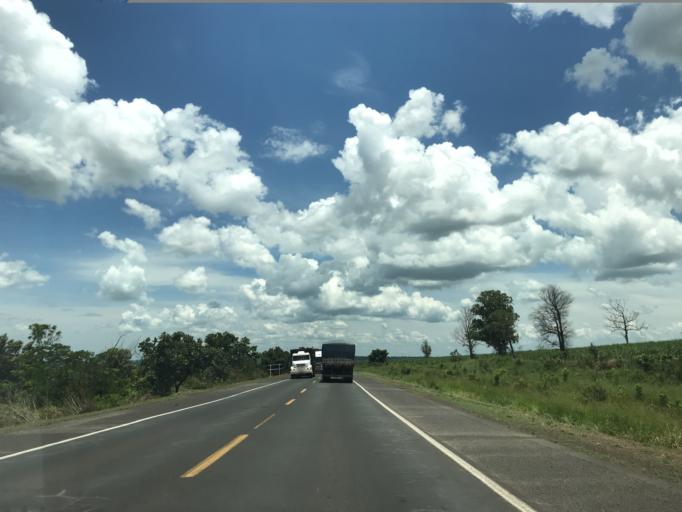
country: BR
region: Minas Gerais
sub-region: Prata
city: Prata
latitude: -19.5434
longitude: -48.8290
